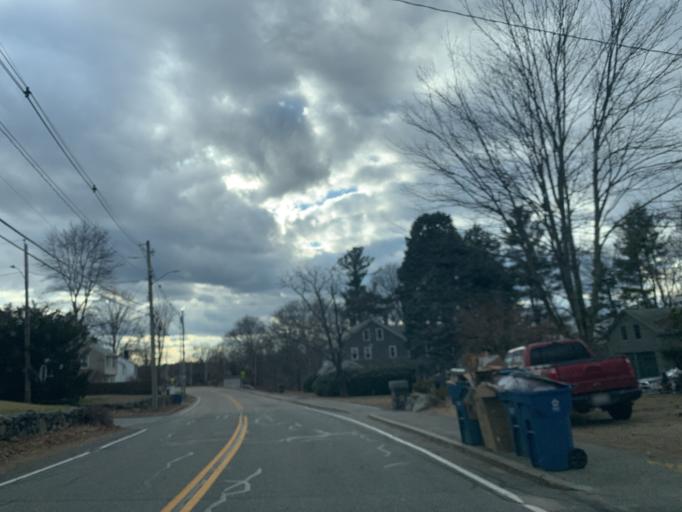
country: US
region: Massachusetts
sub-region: Norfolk County
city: Canton
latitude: 42.1680
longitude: -71.1529
